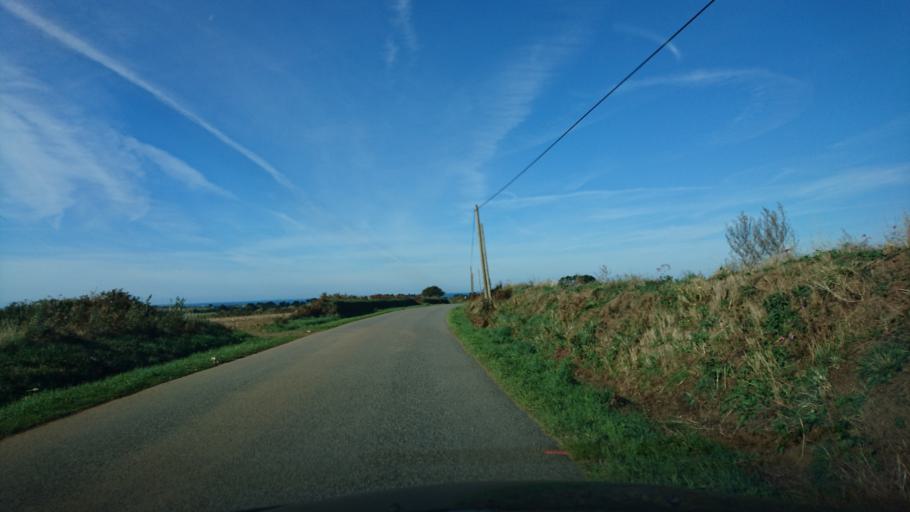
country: FR
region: Brittany
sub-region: Departement du Finistere
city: Plouarzel
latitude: 48.4280
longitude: -4.7531
